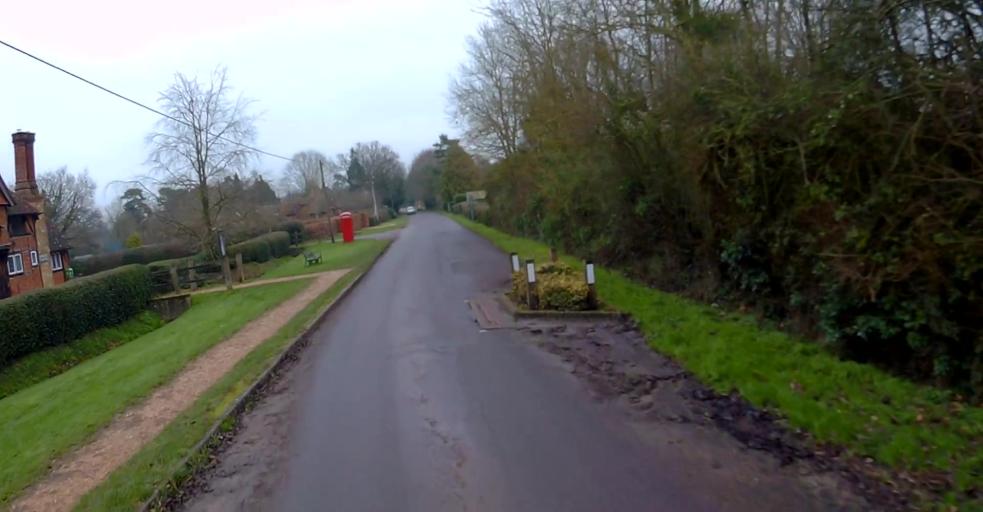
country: GB
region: England
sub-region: Hampshire
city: Hook
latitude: 51.3017
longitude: -0.9769
